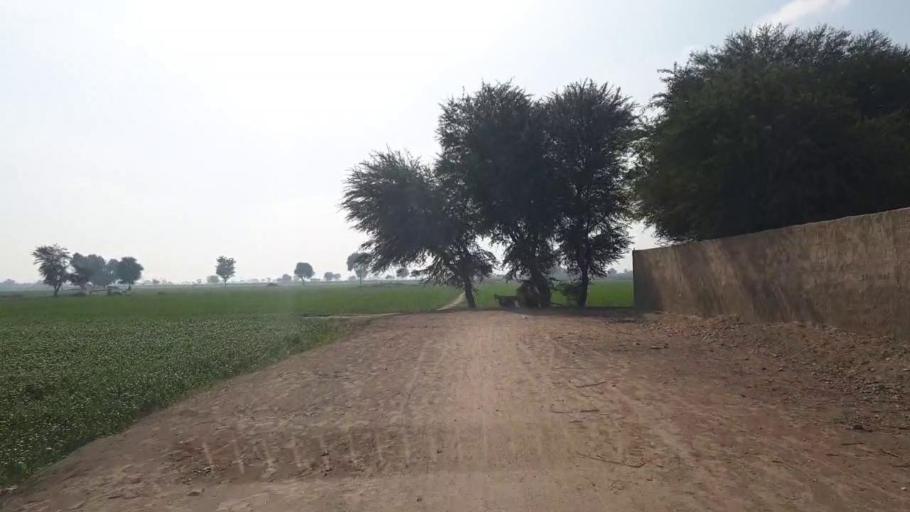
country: PK
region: Sindh
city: Shahdadpur
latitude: 26.0197
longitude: 68.5744
